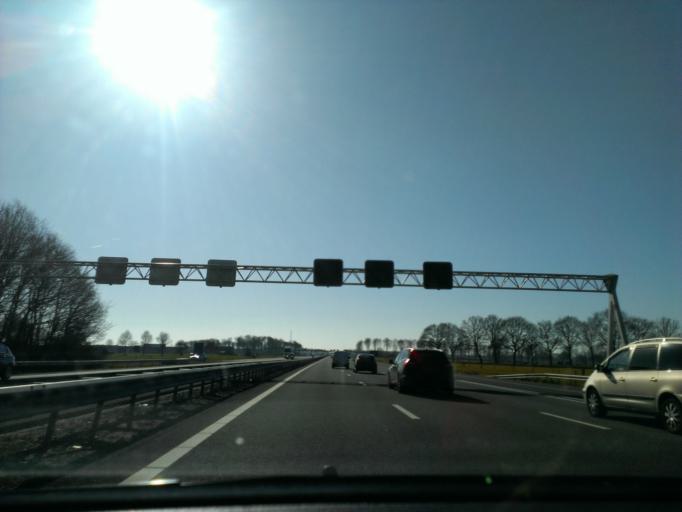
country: NL
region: Overijssel
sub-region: Gemeente Staphorst
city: Staphorst
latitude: 52.6393
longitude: 6.2032
